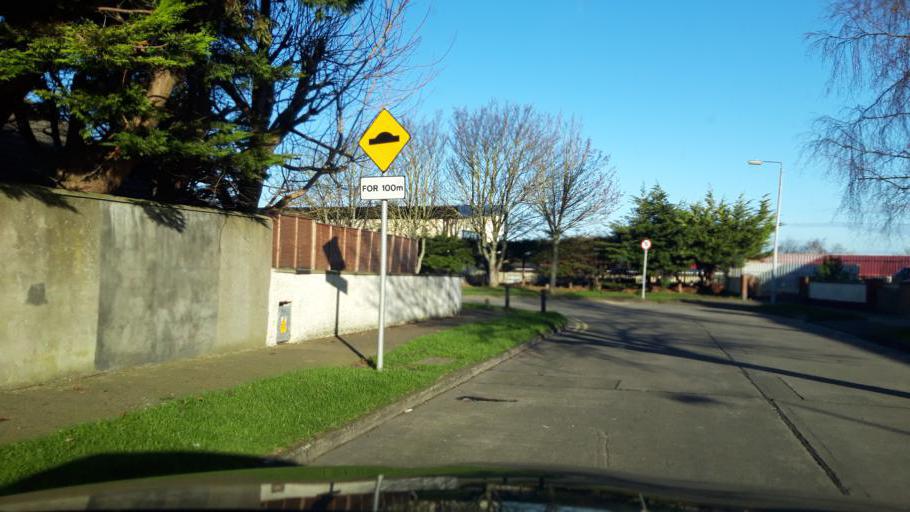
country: IE
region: Leinster
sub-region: Fingal County
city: Swords
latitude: 53.4511
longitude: -6.2424
